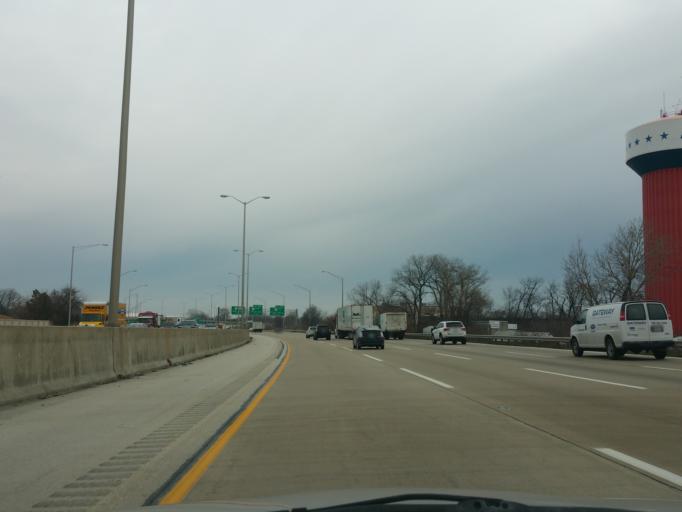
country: US
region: Illinois
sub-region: Cook County
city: Alsip
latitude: 41.6571
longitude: -87.7283
